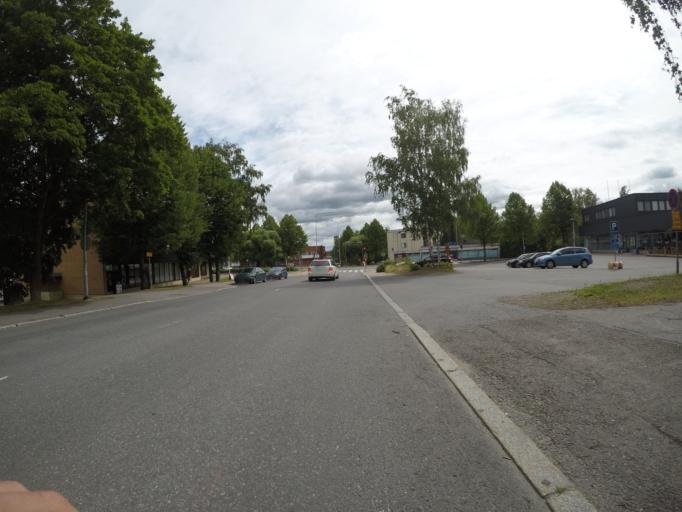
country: FI
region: Haeme
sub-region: Haemeenlinna
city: Haemeenlinna
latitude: 61.0035
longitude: 24.4875
